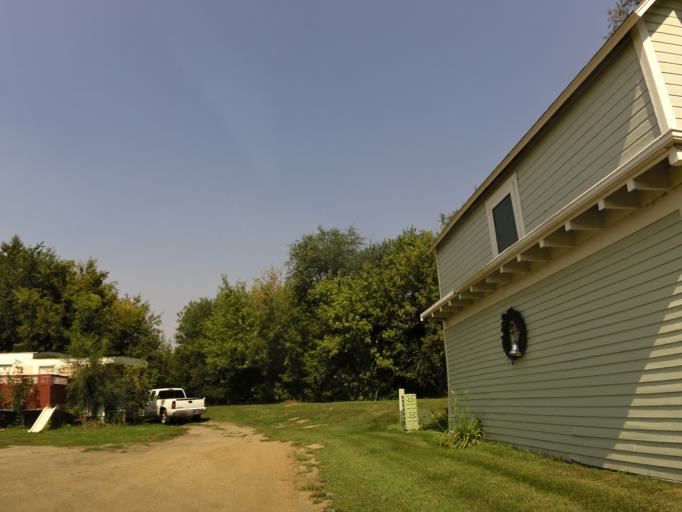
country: US
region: North Dakota
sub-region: Walsh County
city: Grafton
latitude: 48.4213
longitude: -97.4063
